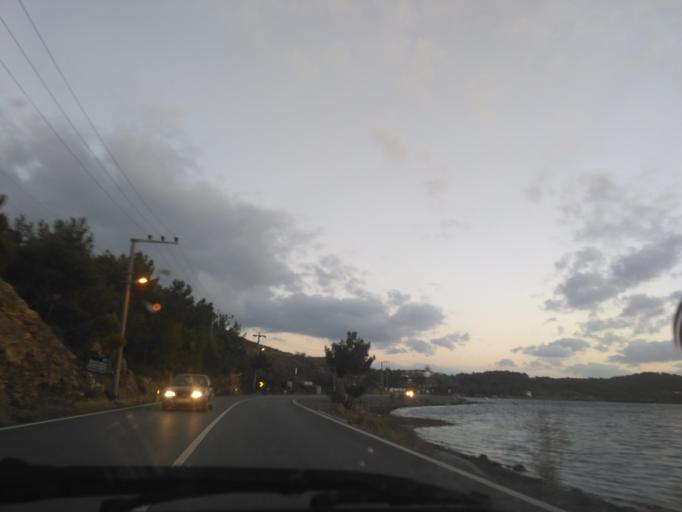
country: TR
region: Balikesir
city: Ayvalik
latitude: 39.2891
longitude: 26.6712
